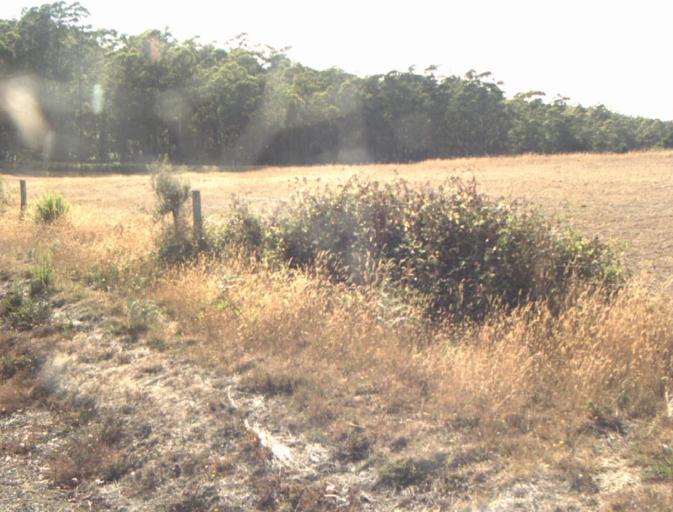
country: AU
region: Tasmania
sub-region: Dorset
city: Bridport
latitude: -41.1494
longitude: 147.2320
